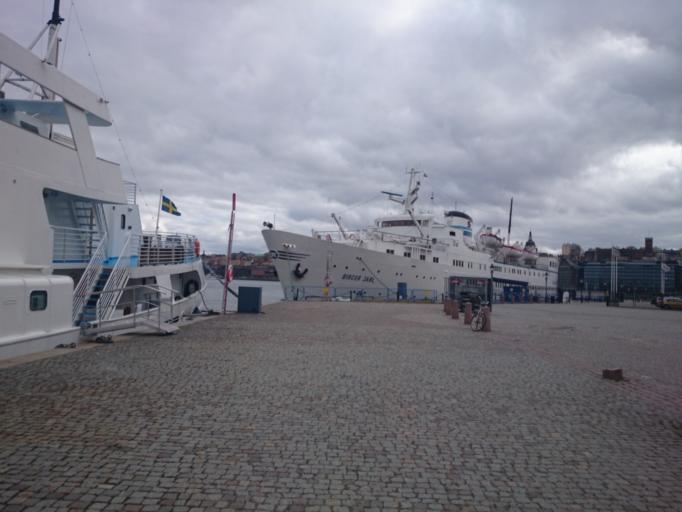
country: SE
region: Stockholm
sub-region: Stockholms Kommun
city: Stockholm
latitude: 59.3255
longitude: 18.0763
